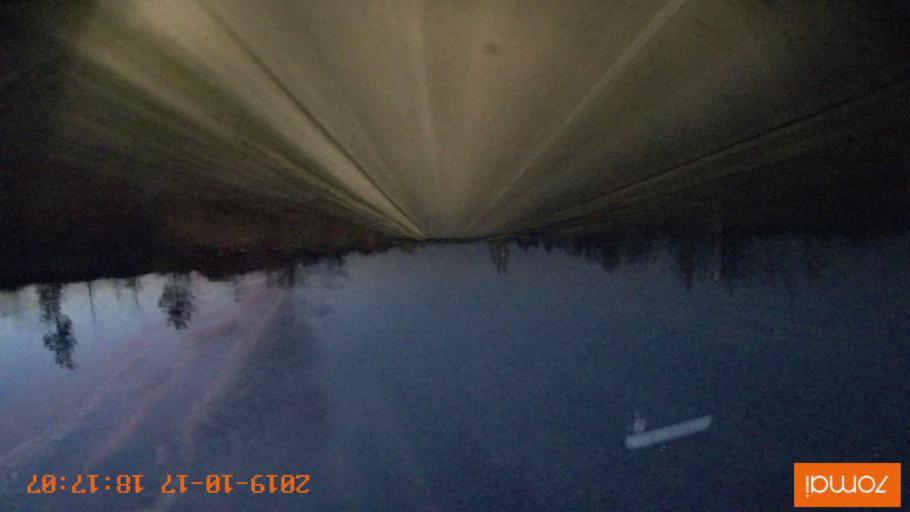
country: RU
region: Tula
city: Kurkino
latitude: 53.3935
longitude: 38.5072
